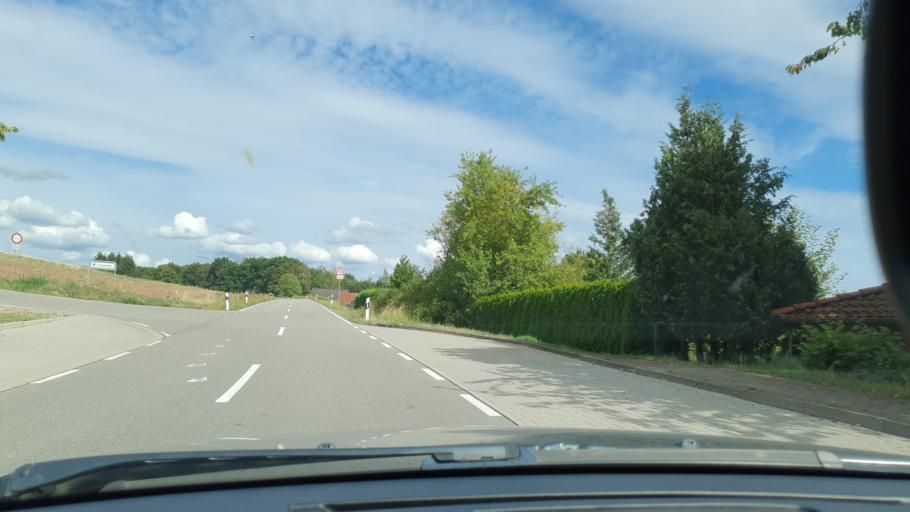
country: DE
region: Rheinland-Pfalz
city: Thaleischweiler-Froschen
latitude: 49.2691
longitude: 7.5866
